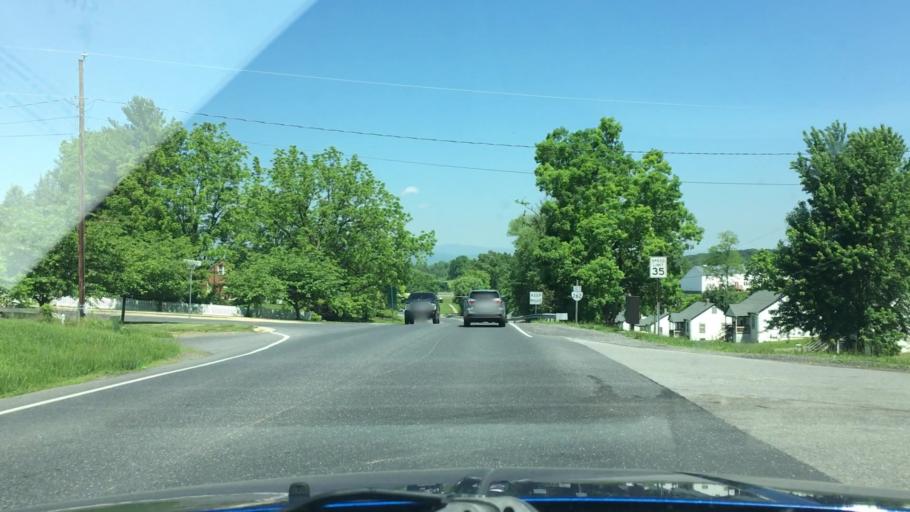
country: US
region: Virginia
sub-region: City of Staunton
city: Staunton
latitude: 38.1776
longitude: -79.0930
